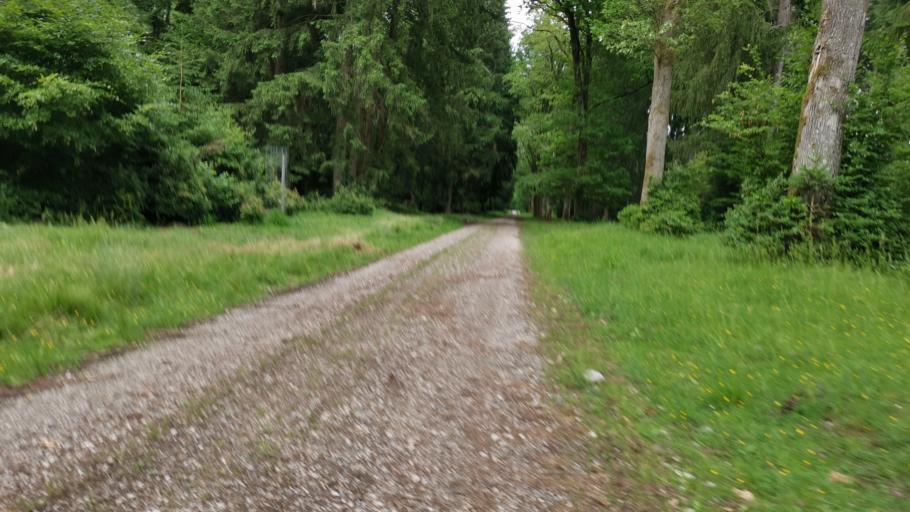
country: DE
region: Bavaria
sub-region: Upper Bavaria
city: Schaftlarn
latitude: 48.0240
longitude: 11.4461
